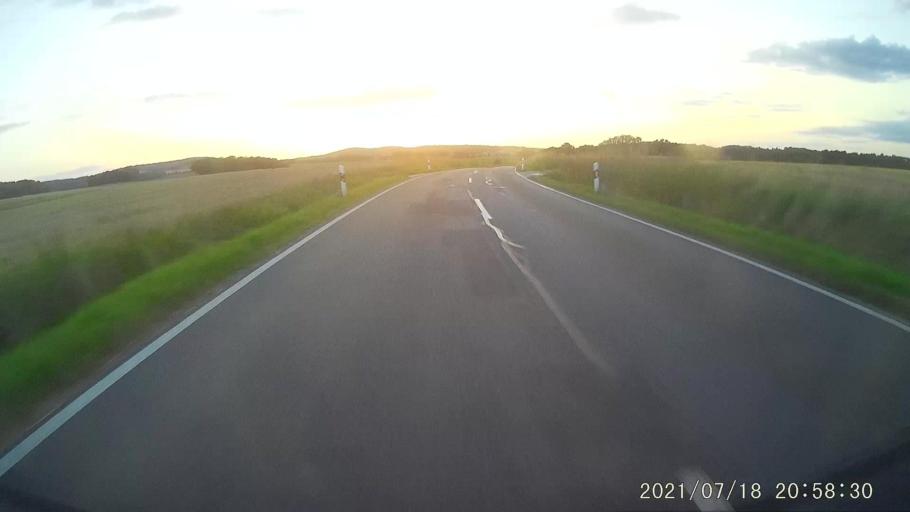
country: DE
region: Saxony
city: Konigshain
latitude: 51.1708
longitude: 14.9117
